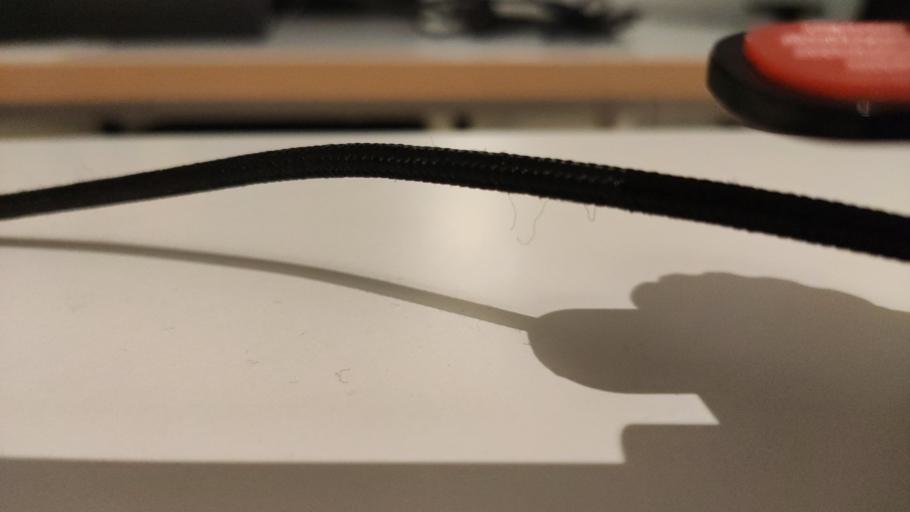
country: RU
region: Moskovskaya
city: Novosin'kovo
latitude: 56.3904
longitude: 37.3049
